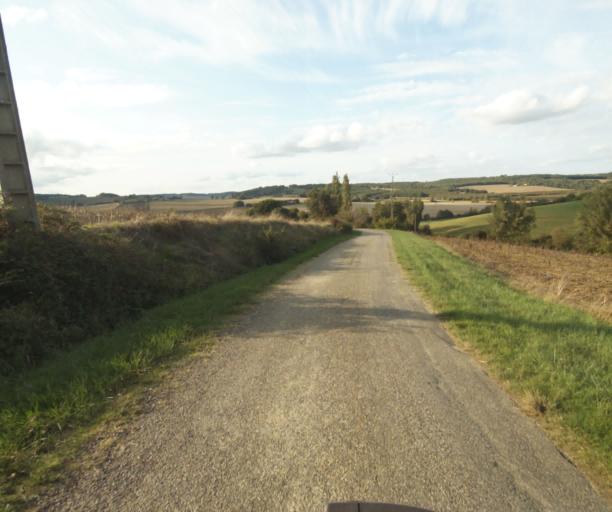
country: FR
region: Midi-Pyrenees
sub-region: Departement de la Haute-Garonne
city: Launac
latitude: 43.8170
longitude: 1.0919
